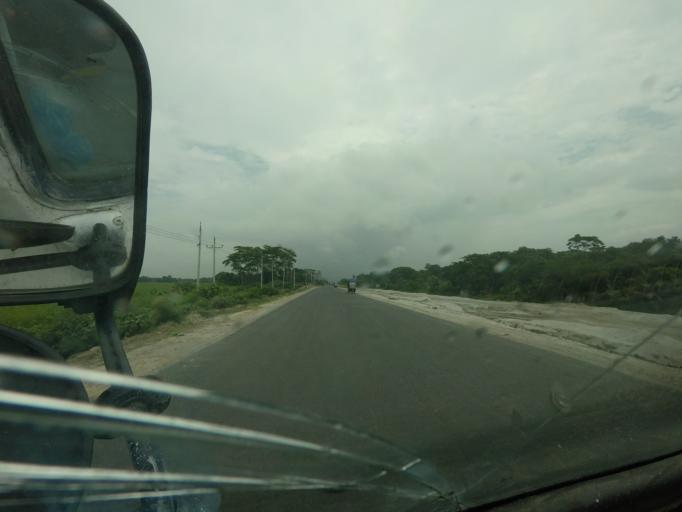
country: BD
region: Dhaka
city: Char Bhadrasan
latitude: 23.3739
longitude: 90.0271
